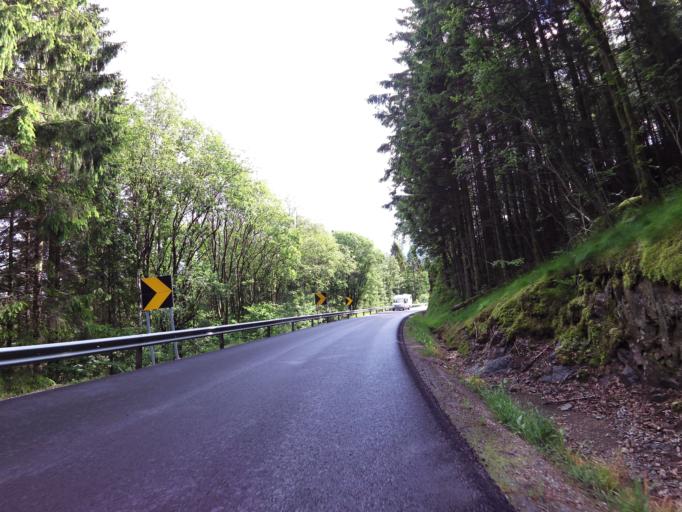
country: NO
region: Vest-Agder
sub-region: Lindesnes
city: Vigeland
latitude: 58.0600
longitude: 7.2231
